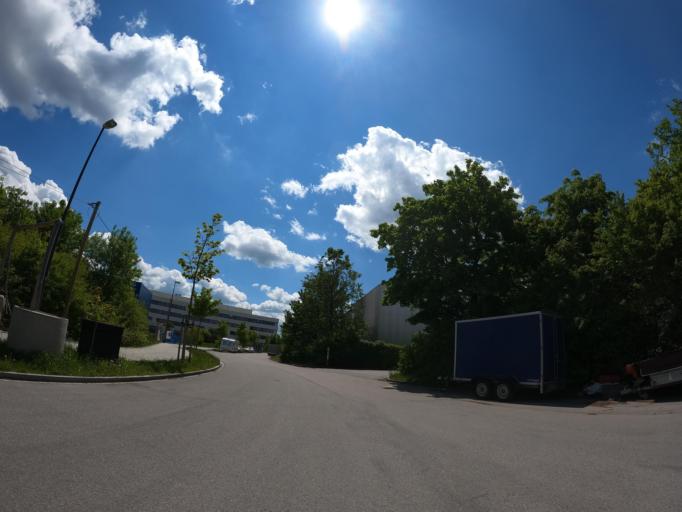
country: DE
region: Bavaria
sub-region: Upper Bavaria
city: Putzbrunn
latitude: 48.0763
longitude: 11.7246
